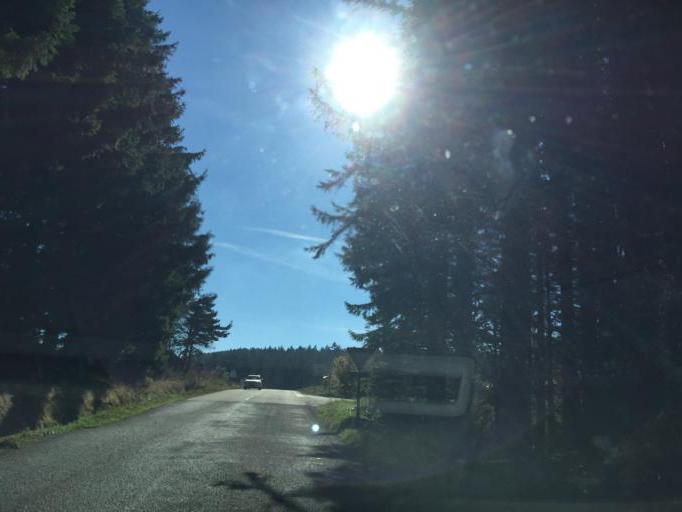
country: FR
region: Rhone-Alpes
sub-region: Departement de la Loire
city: Bourg-Argental
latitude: 45.3696
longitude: 4.5283
